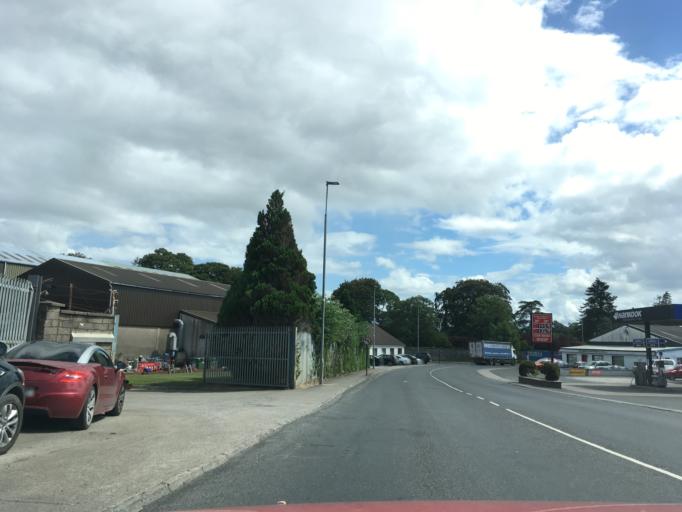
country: IE
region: Munster
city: Cahir
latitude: 52.3745
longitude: -7.9324
